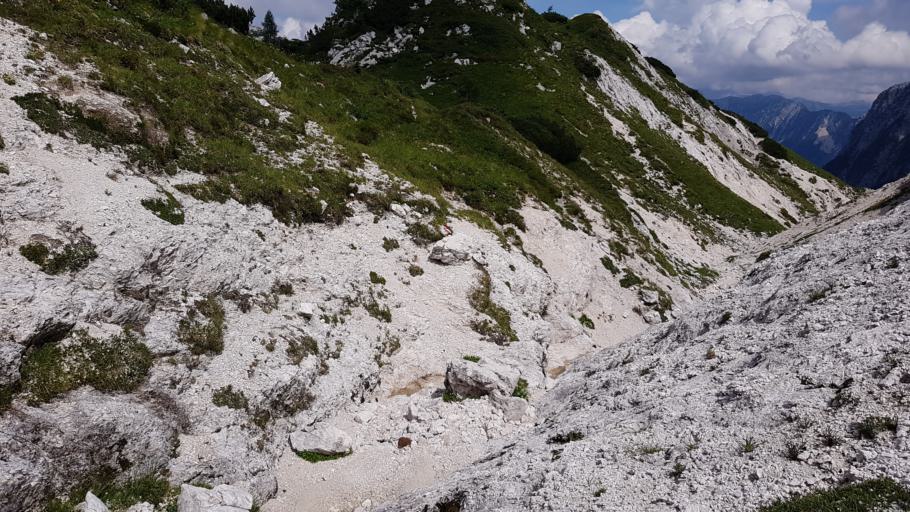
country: SI
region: Bovec
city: Bovec
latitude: 46.3847
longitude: 13.5200
